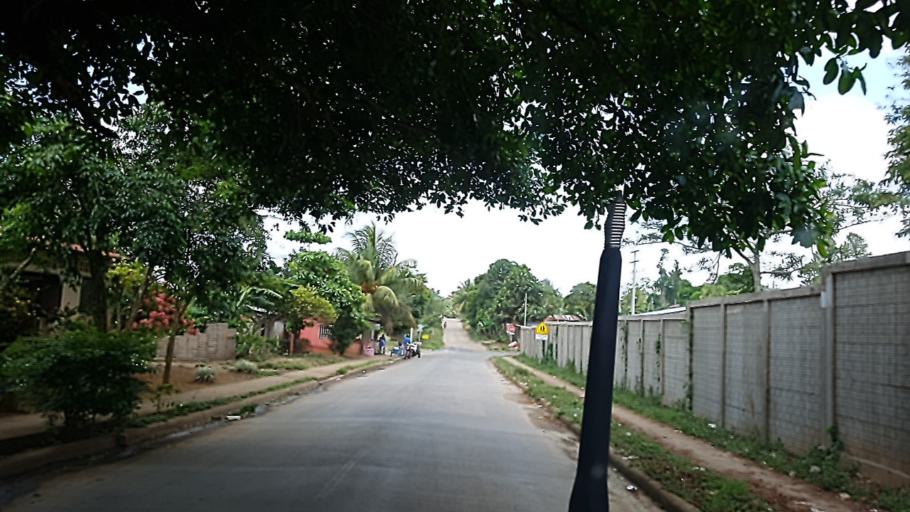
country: NI
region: Atlantico Sur
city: Nueva Guinea
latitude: 11.6859
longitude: -84.4598
